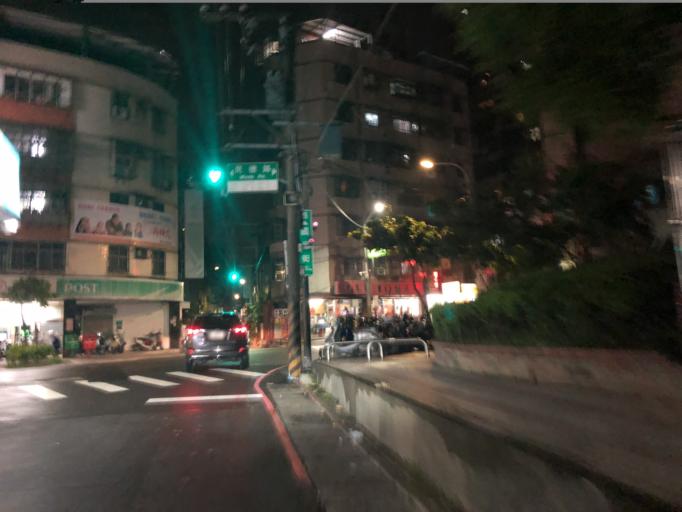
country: TW
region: Taipei
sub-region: Taipei
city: Banqiao
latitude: 25.0009
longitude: 121.4693
